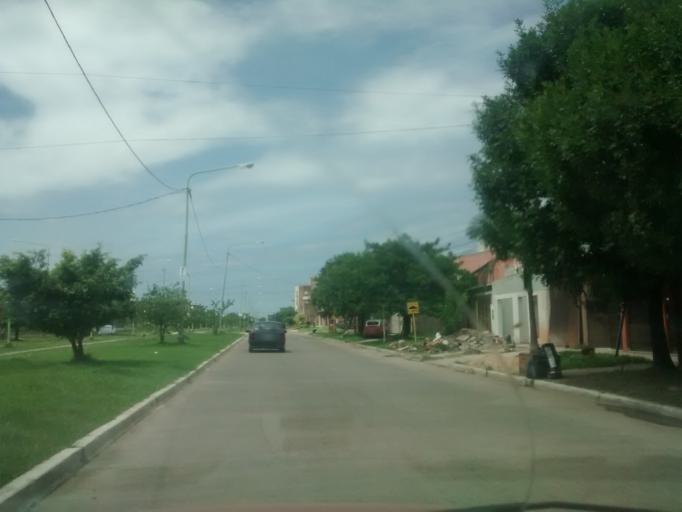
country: AR
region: Chaco
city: Resistencia
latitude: -27.4665
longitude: -58.9876
